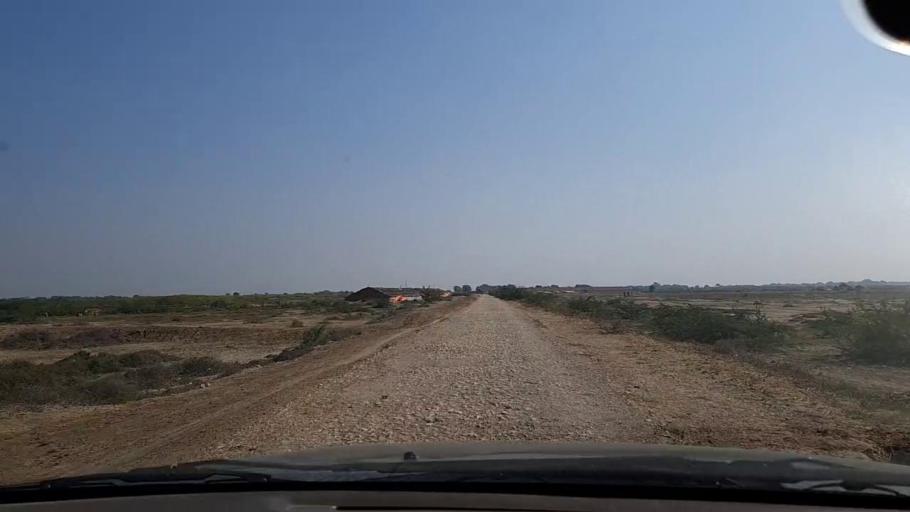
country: PK
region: Sindh
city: Chuhar Jamali
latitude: 24.4207
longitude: 67.8239
